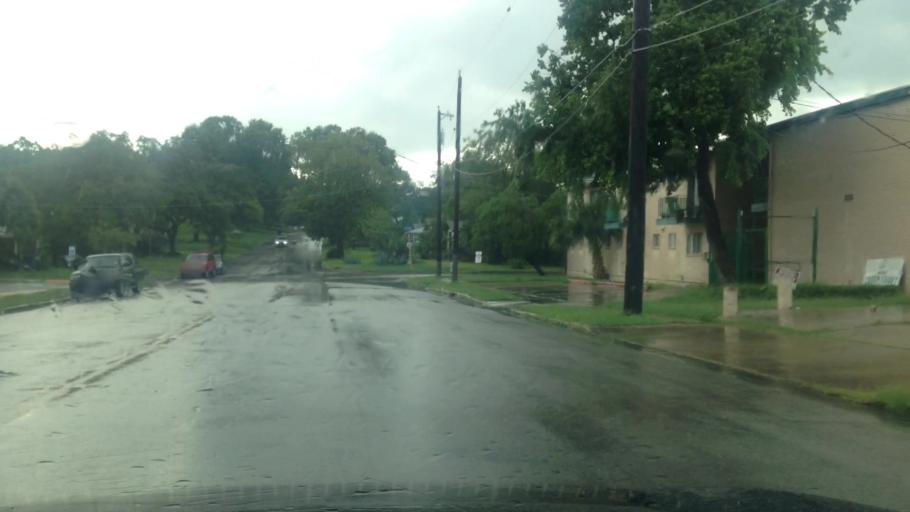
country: US
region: Texas
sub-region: Bexar County
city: Balcones Heights
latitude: 29.4813
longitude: -98.5432
